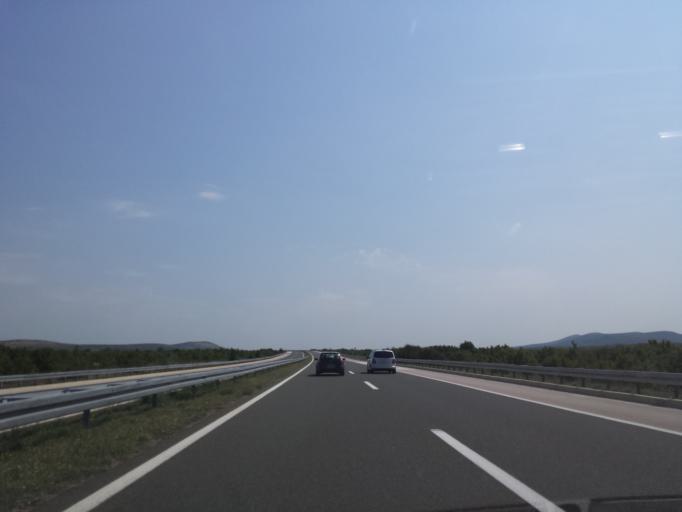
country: HR
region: Zadarska
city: Benkovac
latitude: 43.9621
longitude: 15.6614
